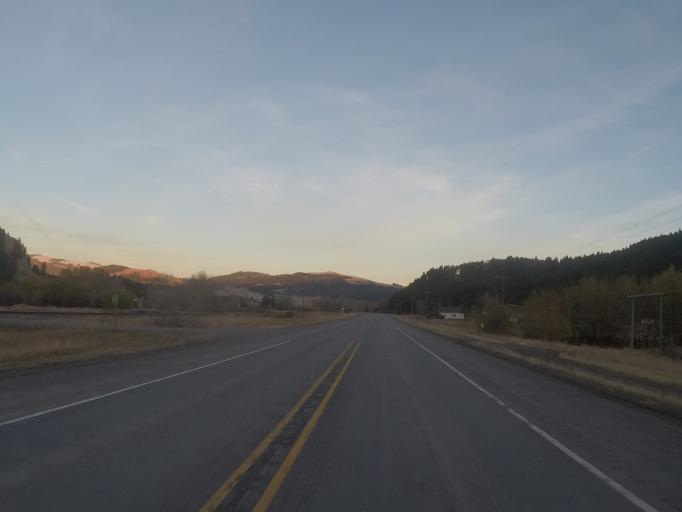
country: US
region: Montana
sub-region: Lewis and Clark County
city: Helena West Side
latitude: 46.5592
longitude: -112.4247
